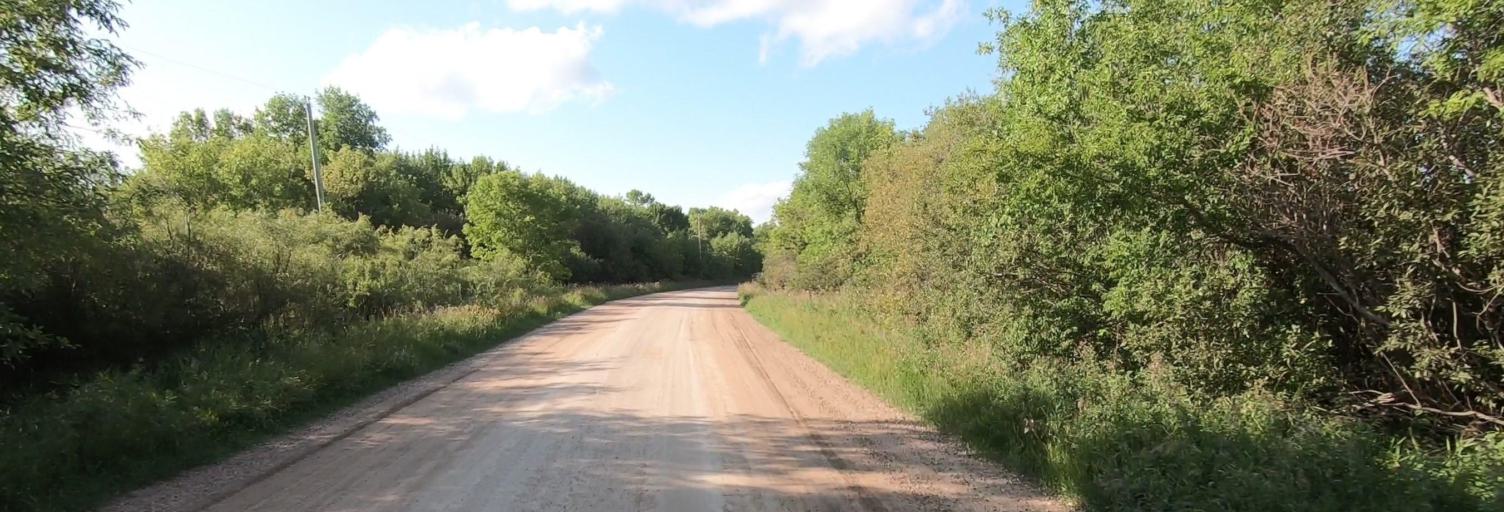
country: CA
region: Manitoba
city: Selkirk
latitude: 50.2513
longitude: -96.8478
